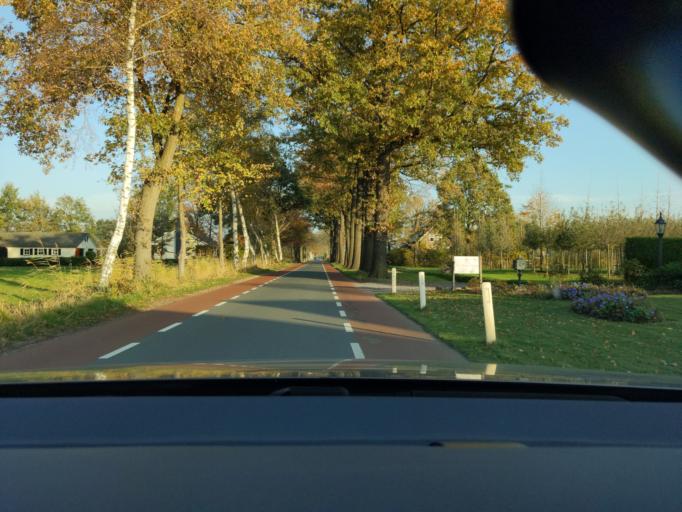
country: NL
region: North Brabant
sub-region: Gemeente Sint-Oedenrode
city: Sint-Oedenrode
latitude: 51.5845
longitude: 5.4455
